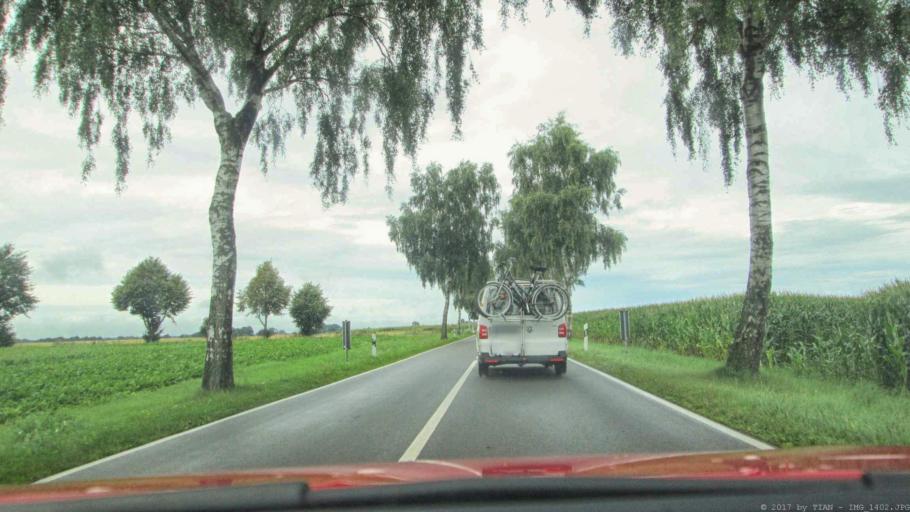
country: DE
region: Lower Saxony
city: Wittingen
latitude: 52.7526
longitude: 10.7215
